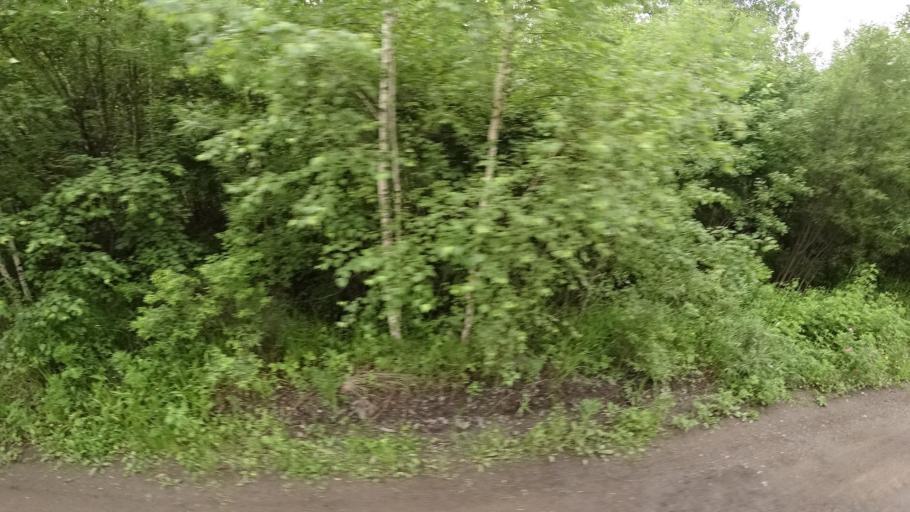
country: RU
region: Khabarovsk Krai
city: Amursk
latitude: 49.9100
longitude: 136.1524
